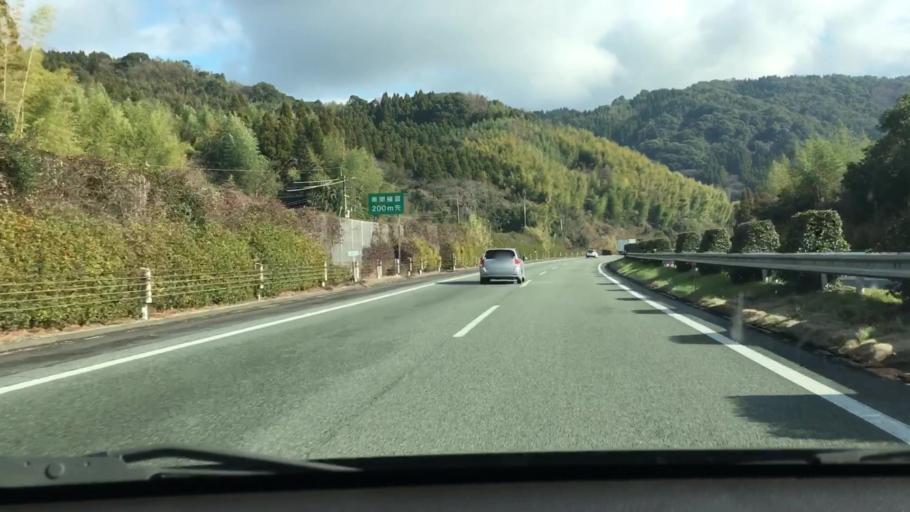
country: JP
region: Kumamoto
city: Matsubase
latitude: 32.6172
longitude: 130.7195
